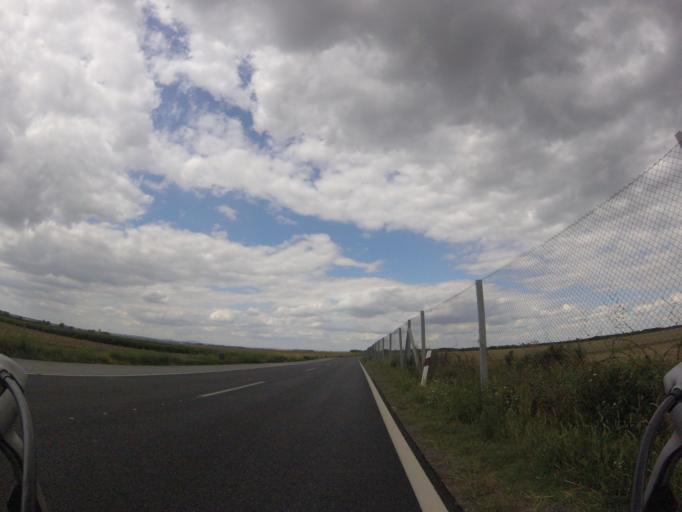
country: HU
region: Baranya
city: Mohacs
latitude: 45.9087
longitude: 18.6595
